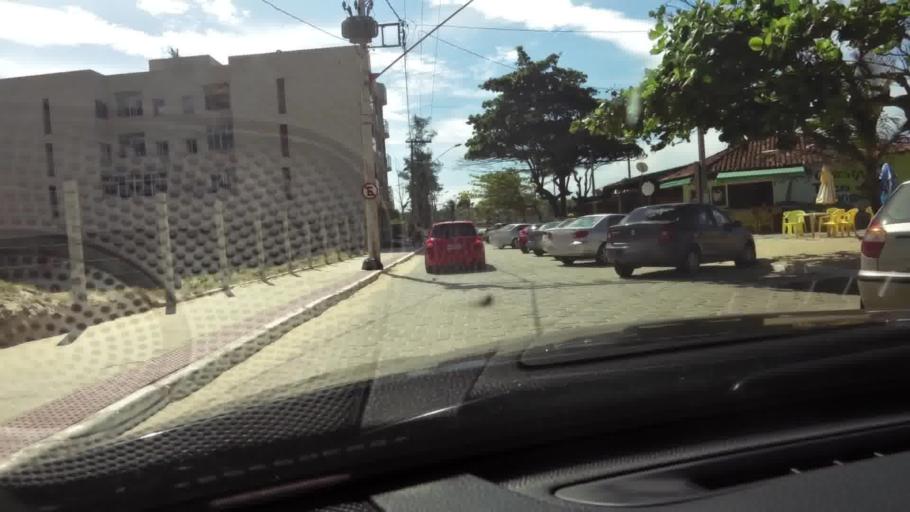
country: BR
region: Espirito Santo
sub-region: Guarapari
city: Guarapari
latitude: -20.6535
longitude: -40.4726
